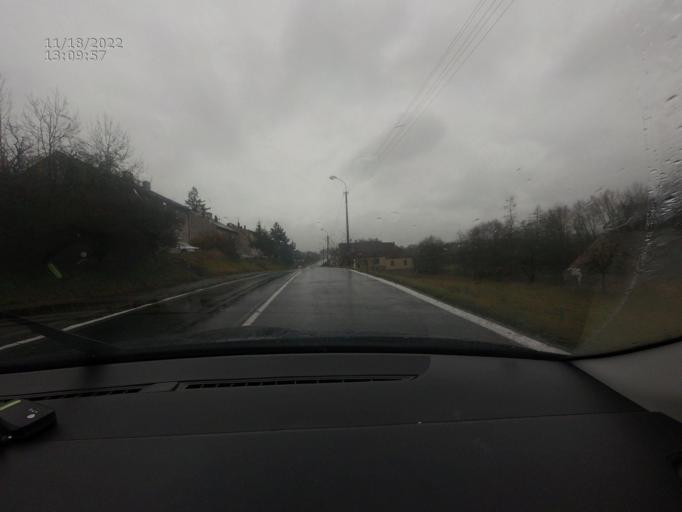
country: CZ
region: Plzensky
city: Hradek
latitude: 49.3342
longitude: 13.5535
